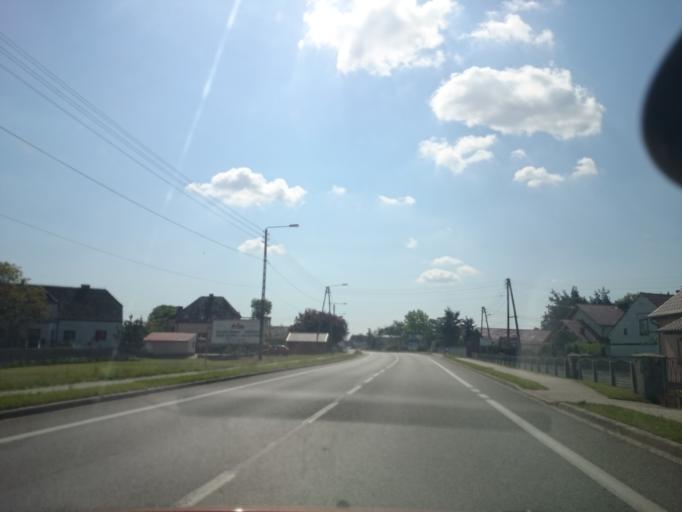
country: PL
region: Opole Voivodeship
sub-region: Powiat opolski
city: Naklo
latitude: 50.5813
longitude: 18.1124
